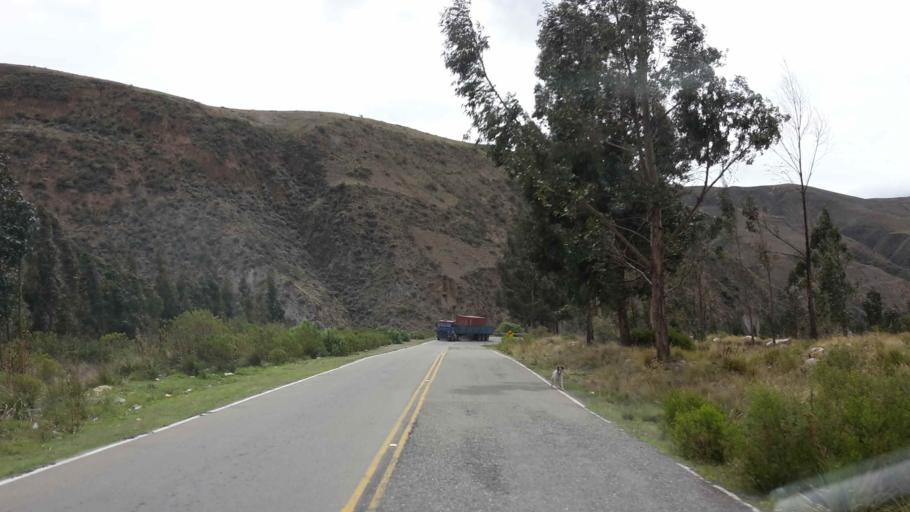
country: BO
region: Cochabamba
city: Colomi
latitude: -17.4138
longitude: -65.7722
